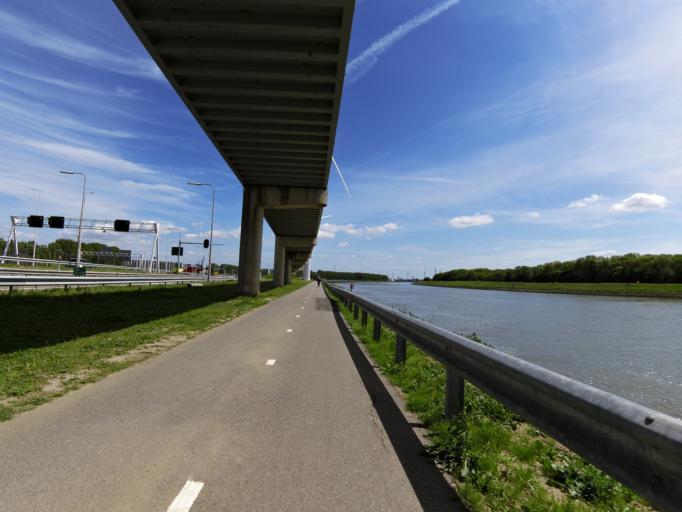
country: NL
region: South Holland
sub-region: Gemeente Maassluis
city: Maassluis
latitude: 51.9019
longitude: 4.2134
